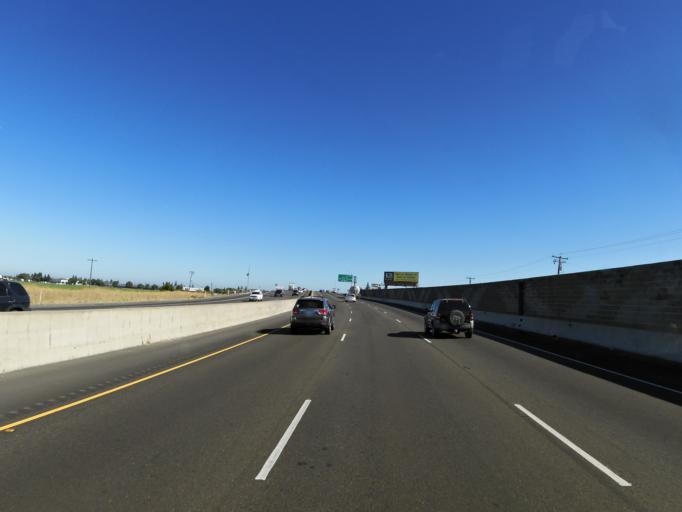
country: US
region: California
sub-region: San Joaquin County
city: Kennedy
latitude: 37.8987
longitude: -121.2204
